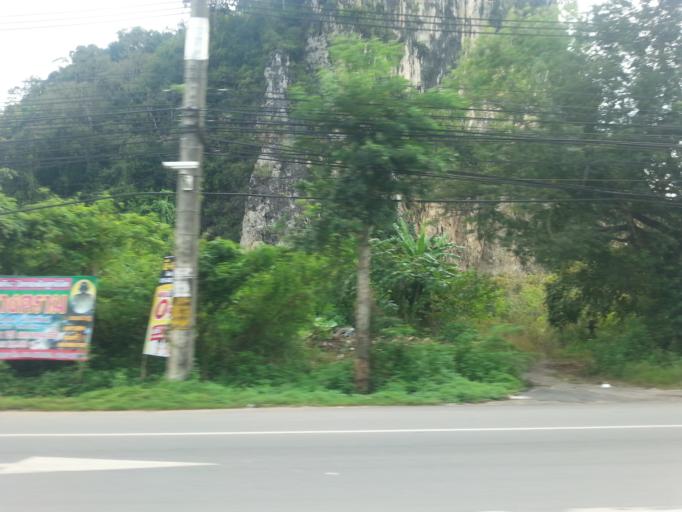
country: TH
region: Krabi
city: Krabi
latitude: 8.1066
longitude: 98.9228
